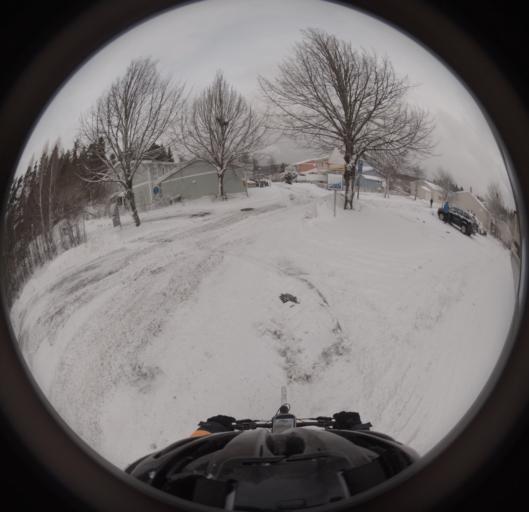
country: SE
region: Stockholm
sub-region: Upplands Vasby Kommun
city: Upplands Vaesby
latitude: 59.4881
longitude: 17.9249
